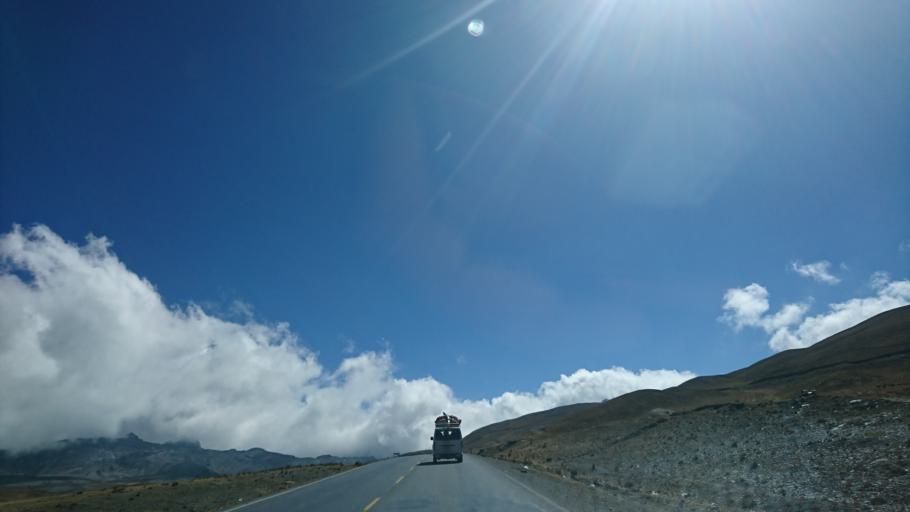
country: BO
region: La Paz
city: La Paz
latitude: -16.3507
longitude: -68.0409
